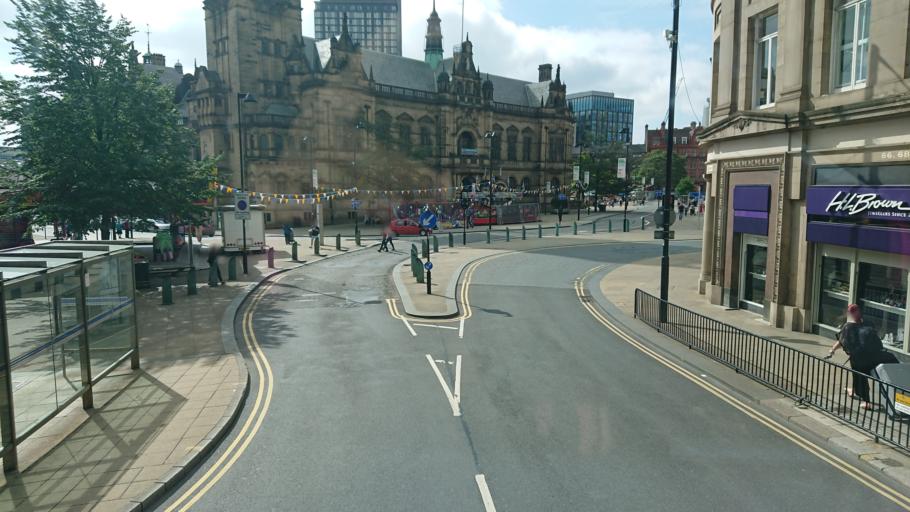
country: GB
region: England
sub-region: Sheffield
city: Sheffield
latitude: 53.3812
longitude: -1.4706
